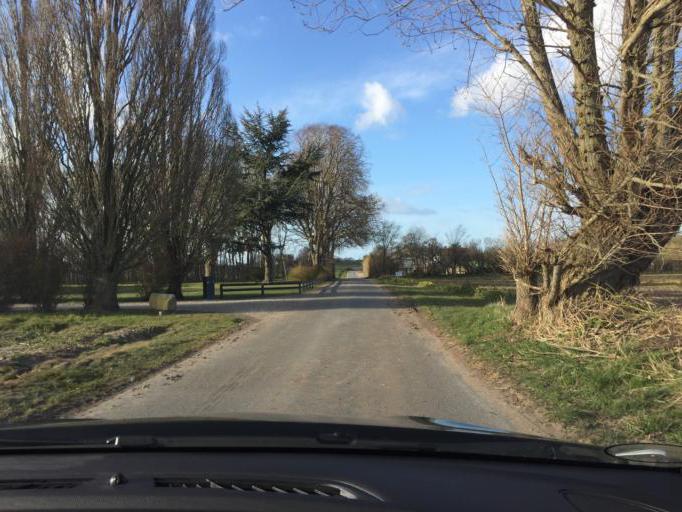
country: DK
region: South Denmark
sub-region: Nyborg Kommune
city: Ullerslev
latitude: 55.3491
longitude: 10.7192
